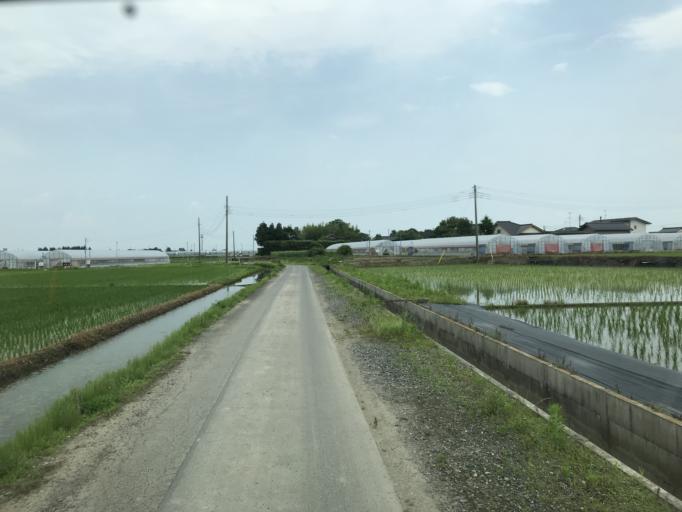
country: JP
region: Saitama
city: Shobu
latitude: 36.0876
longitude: 139.6264
